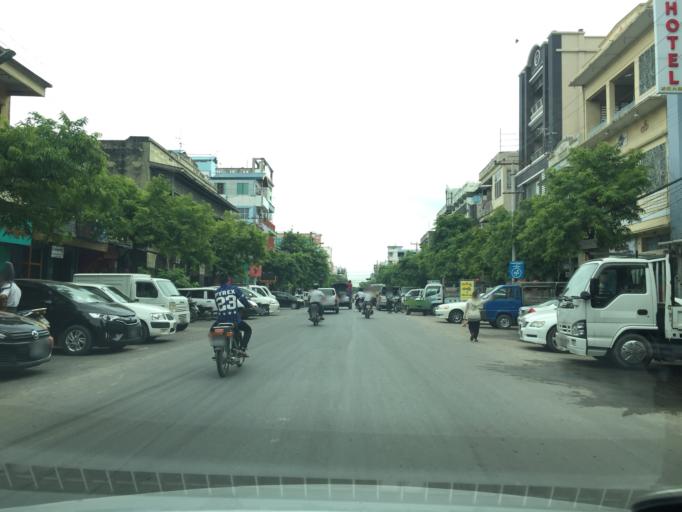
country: MM
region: Mandalay
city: Mandalay
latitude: 21.9822
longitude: 96.0795
